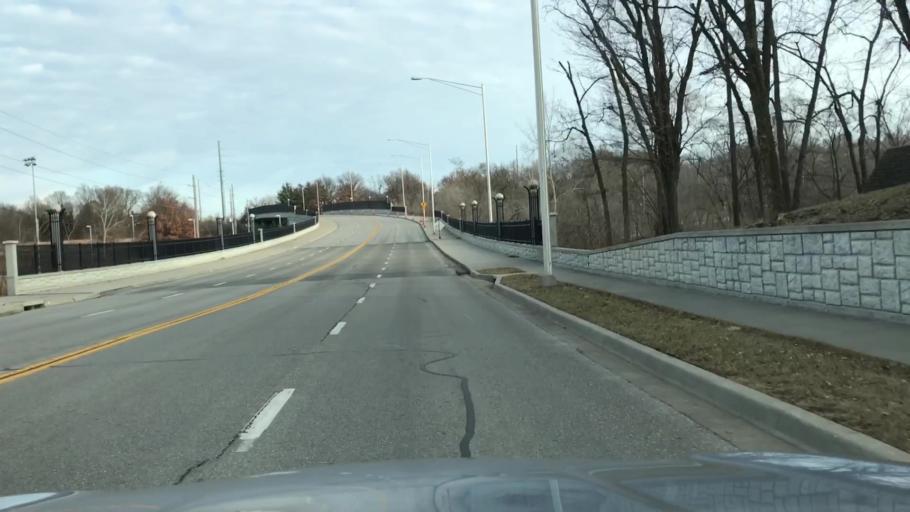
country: US
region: Missouri
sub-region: Jackson County
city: Lees Summit
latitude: 38.9060
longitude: -94.4145
